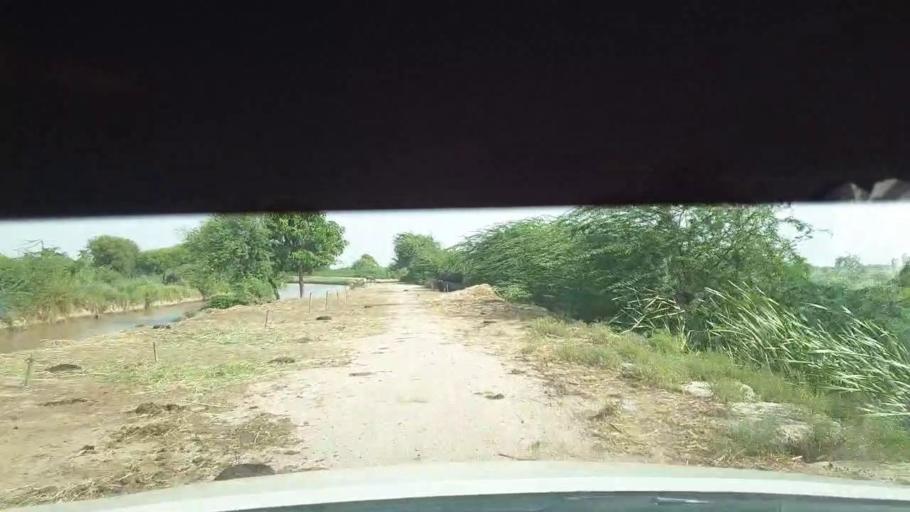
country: PK
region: Sindh
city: Kadhan
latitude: 24.5211
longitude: 69.0036
